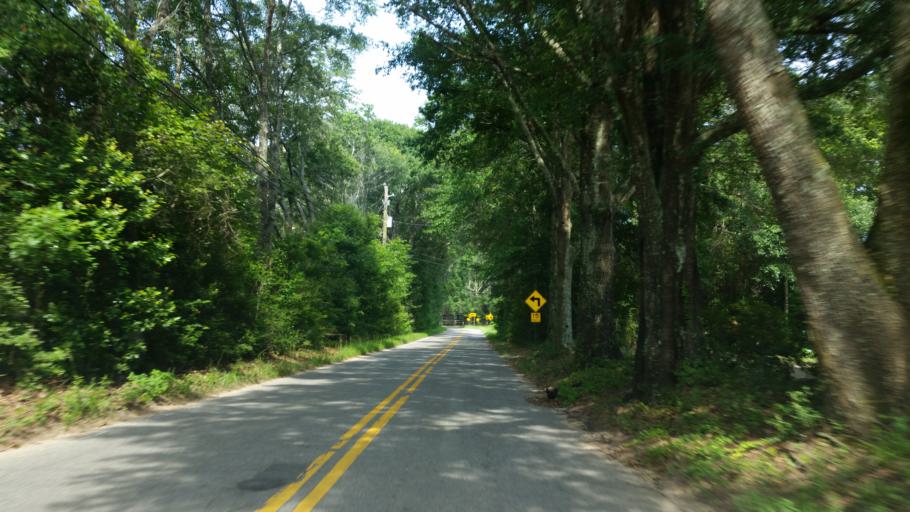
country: US
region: Florida
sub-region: Escambia County
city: Cantonment
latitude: 30.5748
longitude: -87.3595
